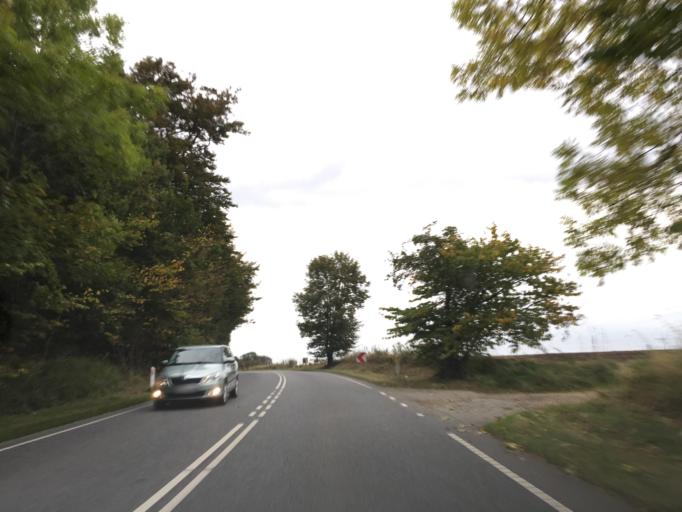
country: DK
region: Central Jutland
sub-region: Viborg Kommune
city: Bjerringbro
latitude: 56.3164
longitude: 9.6874
